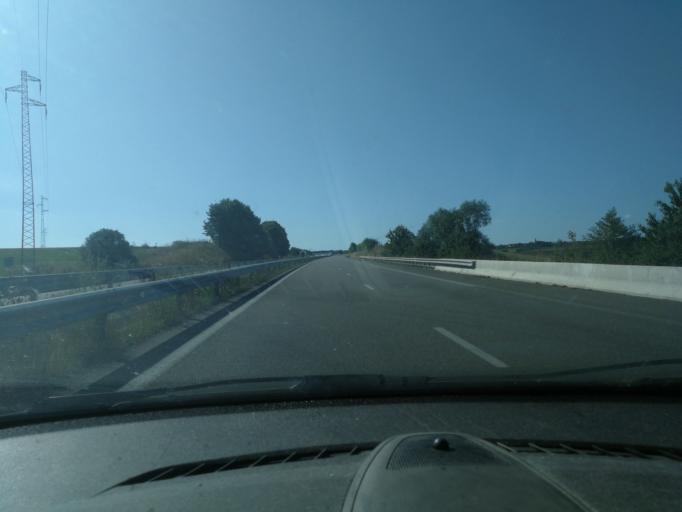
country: FR
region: Lorraine
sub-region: Departement de la Moselle
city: Phalsbourg
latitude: 48.7846
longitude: 7.2245
